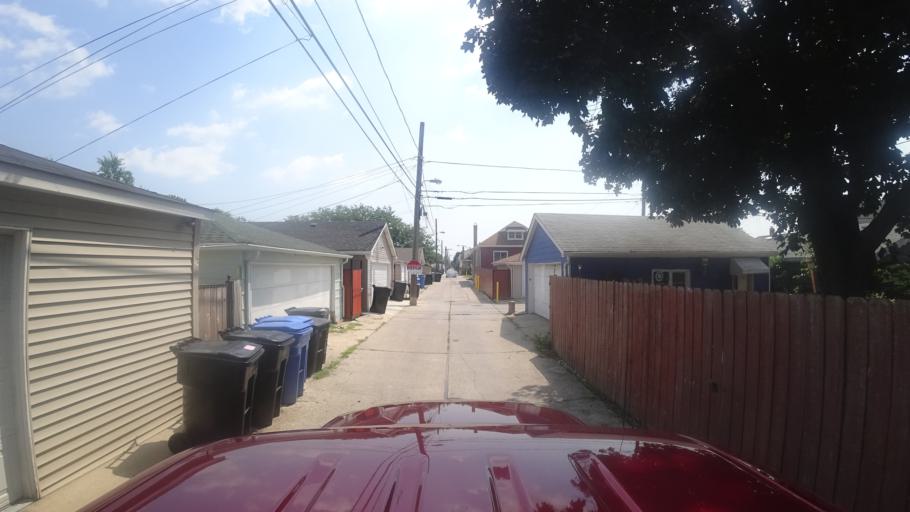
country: US
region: Illinois
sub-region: Cook County
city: Hometown
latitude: 41.7854
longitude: -87.7299
